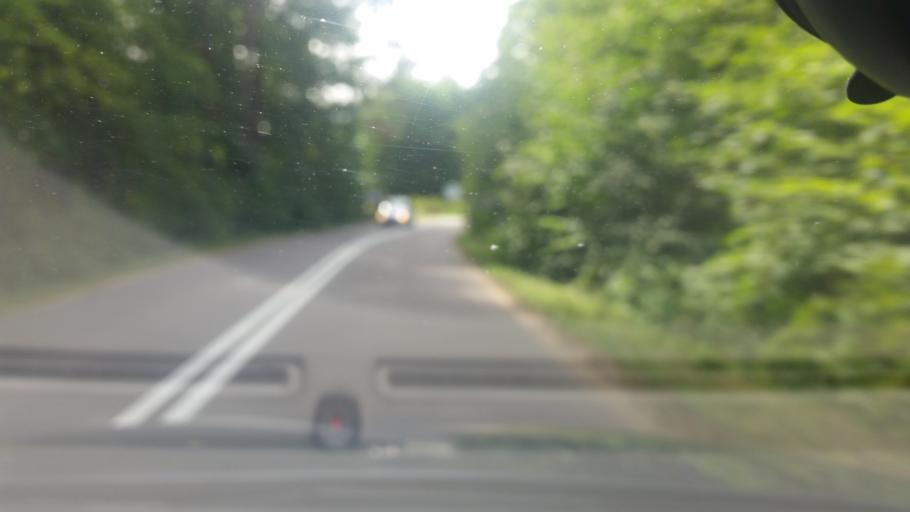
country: PL
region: Pomeranian Voivodeship
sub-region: Powiat wejherowski
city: Choczewo
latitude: 54.7469
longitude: 17.7444
